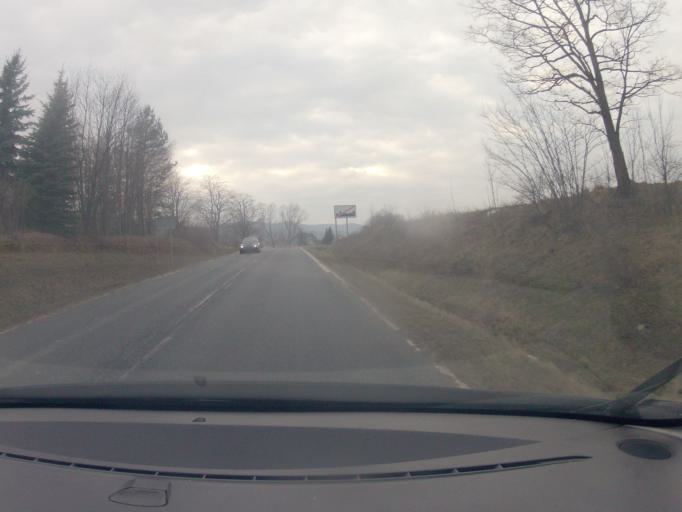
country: PL
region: Subcarpathian Voivodeship
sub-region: Powiat krosnienski
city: Dukla
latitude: 49.5600
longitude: 21.6202
